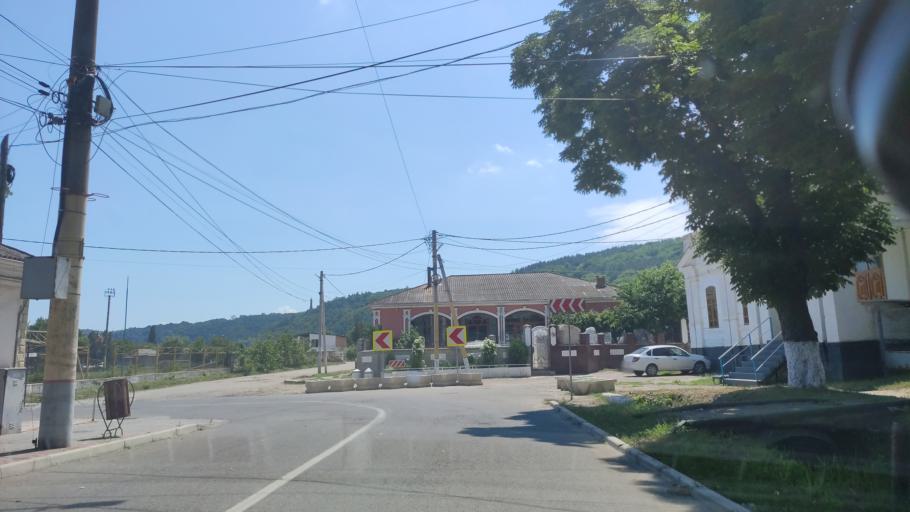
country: MD
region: Raionul Soroca
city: Soroca
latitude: 48.1493
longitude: 28.3002
